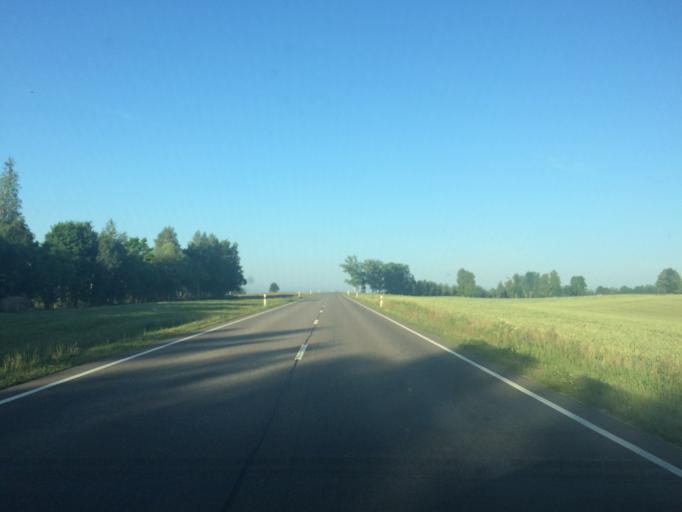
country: LT
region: Utenos apskritis
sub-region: Anyksciai
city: Anyksciai
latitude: 55.4052
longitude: 25.1888
